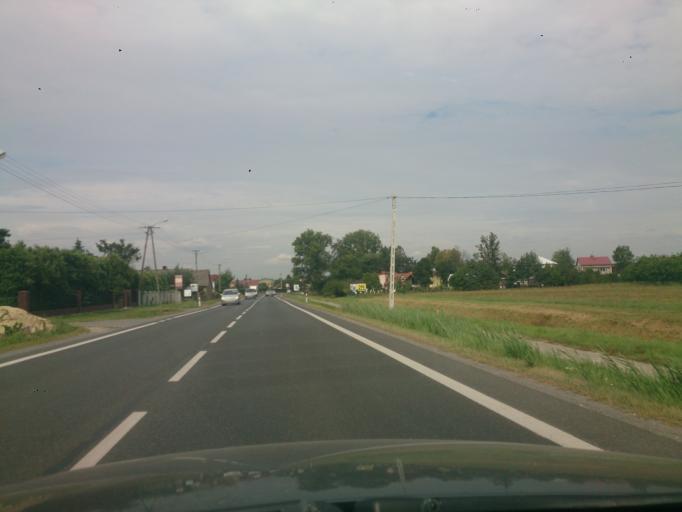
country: PL
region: Subcarpathian Voivodeship
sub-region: Powiat kolbuszowski
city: Kolbuszowa
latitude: 50.2207
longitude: 21.8011
